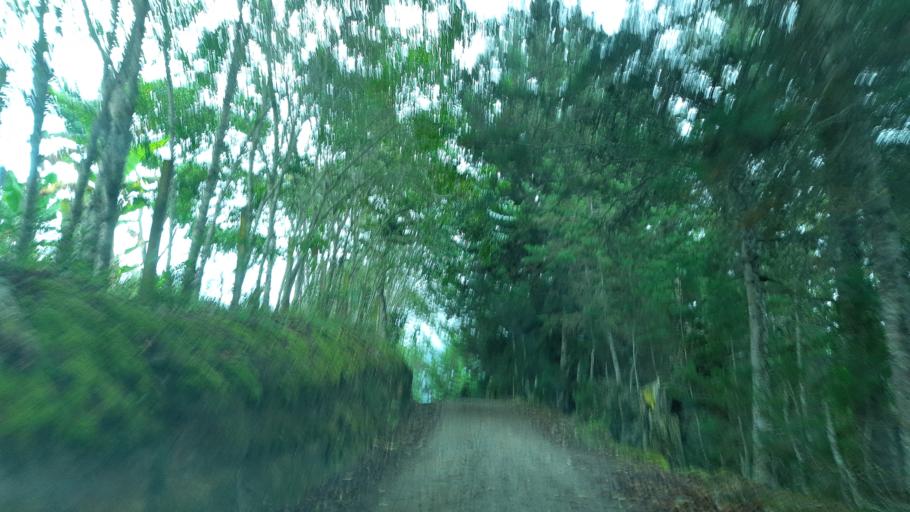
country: CO
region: Boyaca
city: Chinavita
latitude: 5.1363
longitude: -73.3530
